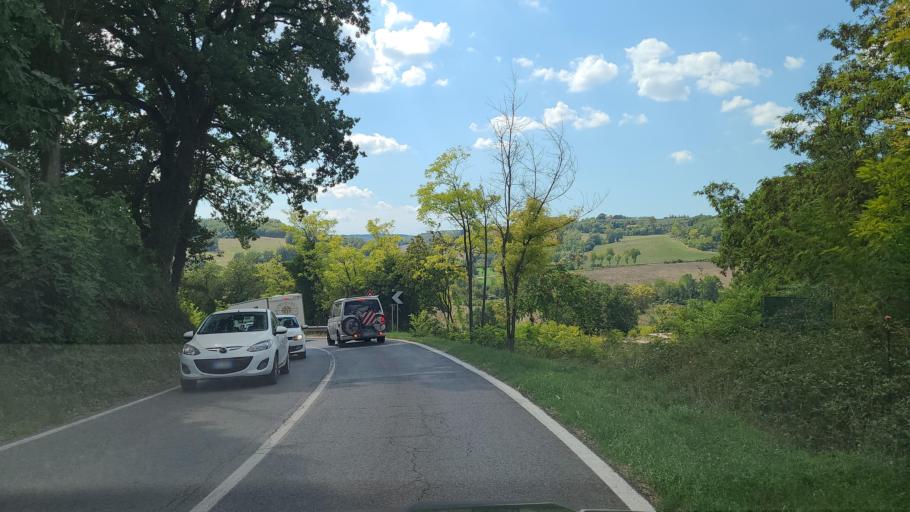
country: IT
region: Tuscany
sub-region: Provincia di Siena
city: Colle di Val d'Elsa
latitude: 43.4132
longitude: 11.0747
